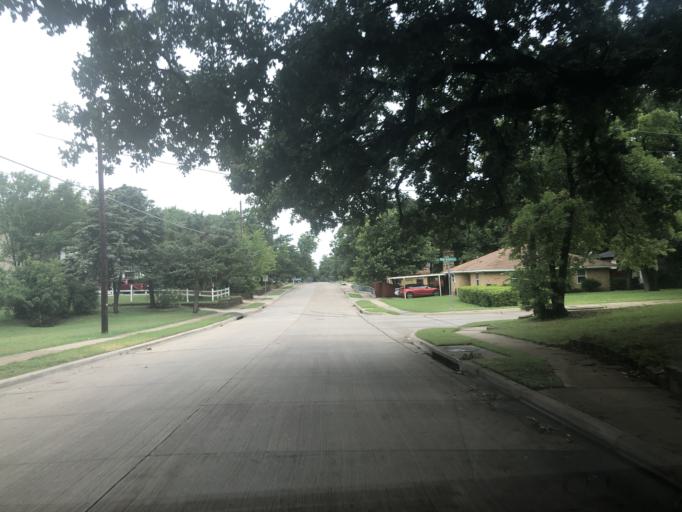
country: US
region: Texas
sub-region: Dallas County
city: Irving
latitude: 32.8031
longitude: -96.9389
